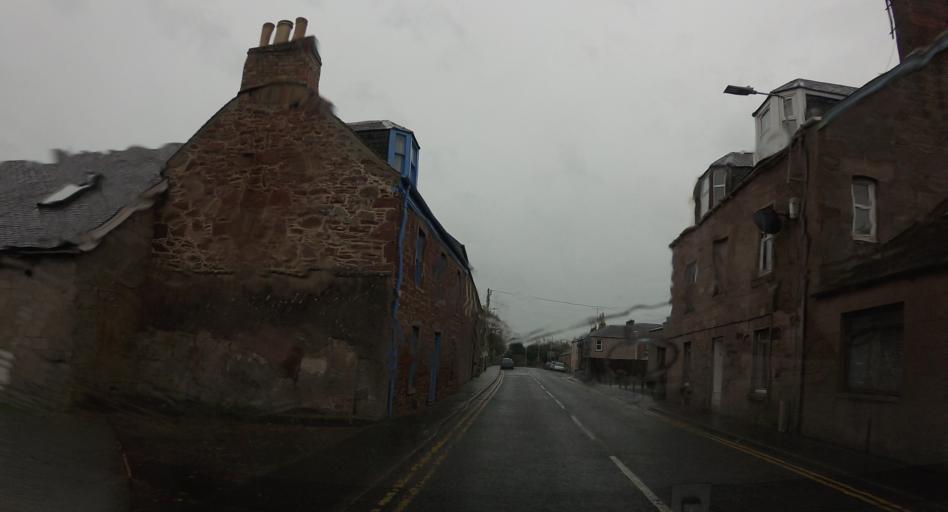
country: GB
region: Scotland
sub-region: Perth and Kinross
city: Coupar Angus
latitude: 56.5443
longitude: -3.2660
